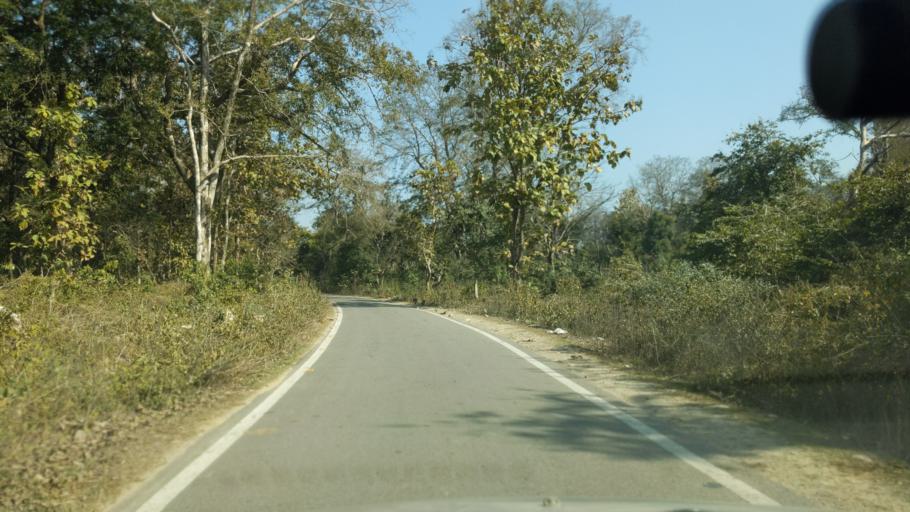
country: IN
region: Uttarakhand
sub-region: Naini Tal
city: Ramnagar
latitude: 29.4112
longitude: 79.1374
